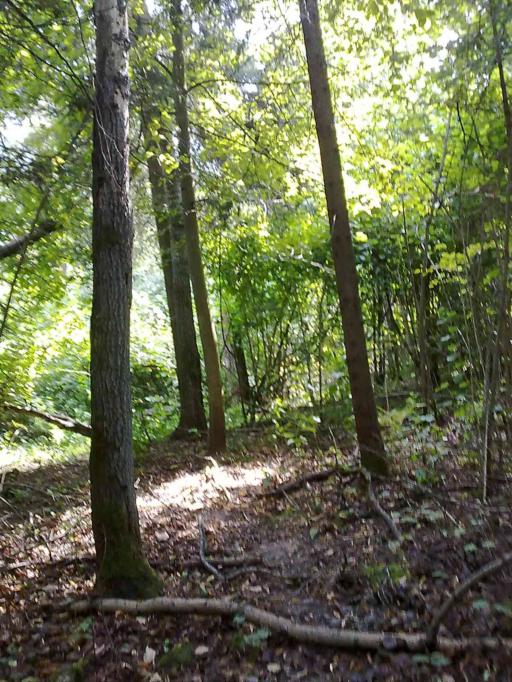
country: RU
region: Moskovskaya
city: Filimonki
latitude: 55.5744
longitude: 37.3631
